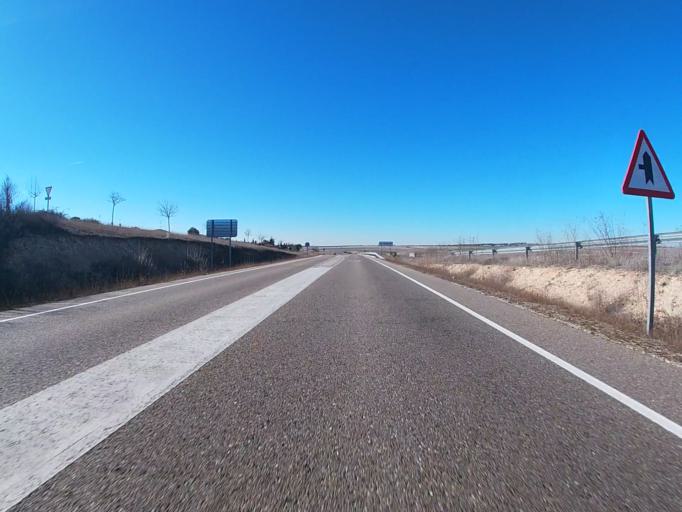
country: ES
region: Castille and Leon
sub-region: Provincia de Salamanca
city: Juzbado
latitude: 41.0794
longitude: -5.8596
